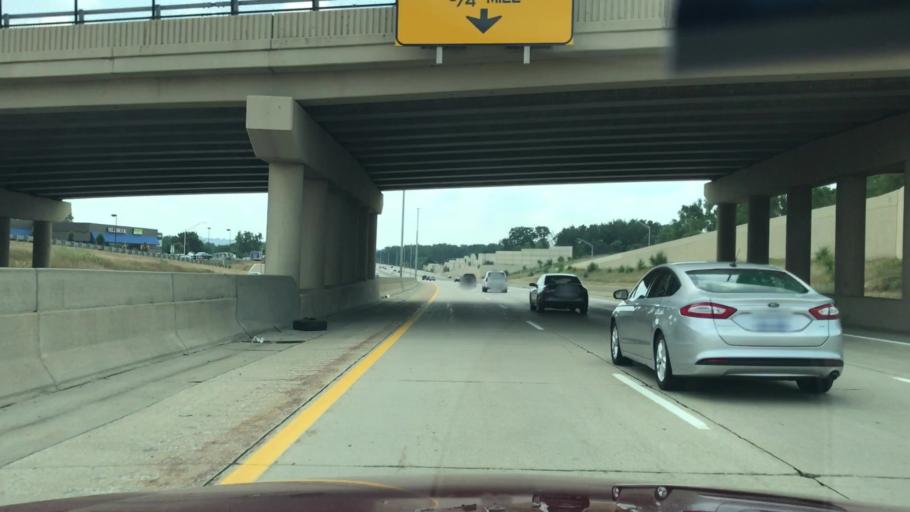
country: US
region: Michigan
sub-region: Kent County
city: Cutlerville
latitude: 42.8413
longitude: -85.6783
